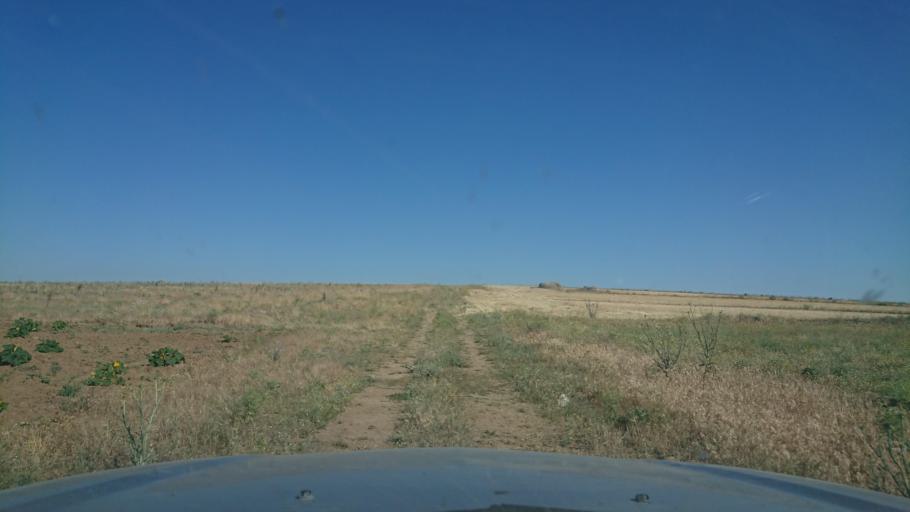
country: TR
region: Aksaray
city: Agacoren
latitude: 38.8376
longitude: 33.9440
